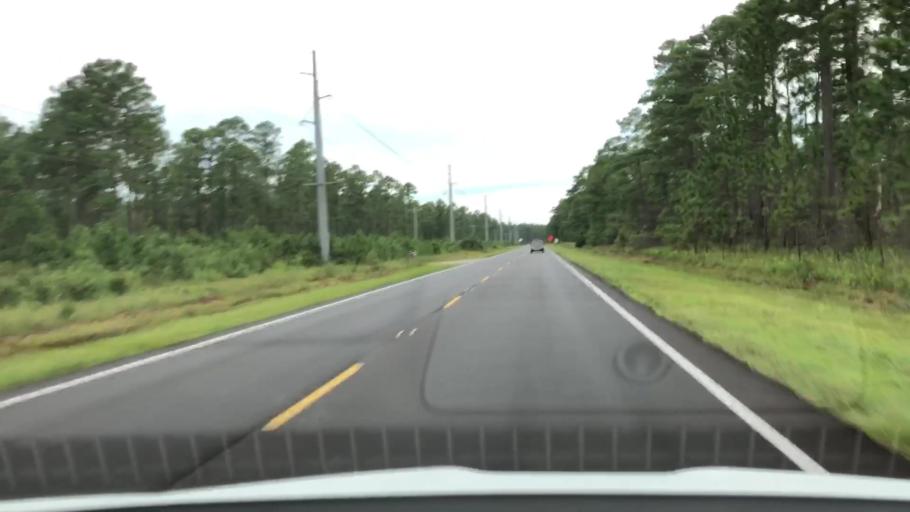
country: US
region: North Carolina
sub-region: Onslow County
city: Swansboro
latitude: 34.8115
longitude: -77.1379
